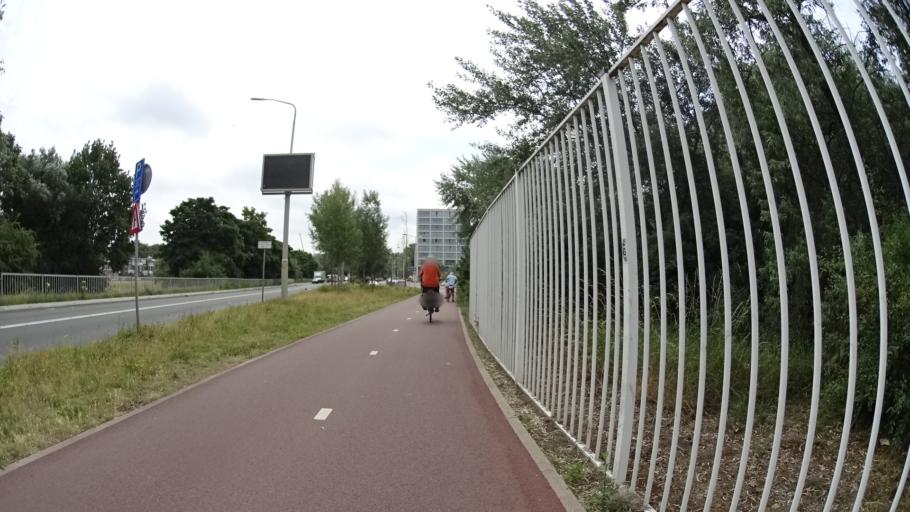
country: NL
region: South Holland
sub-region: Gemeente Den Haag
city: Scheveningen
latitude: 52.0879
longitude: 4.2691
